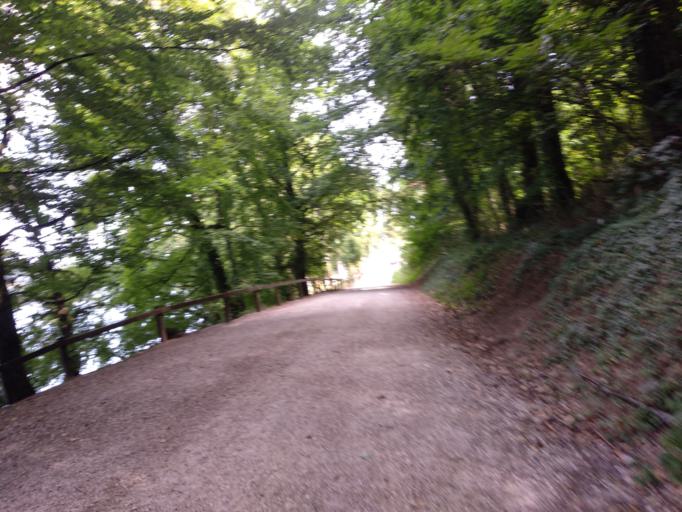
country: FR
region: Rhone-Alpes
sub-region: Departement de l'Isere
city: Charavines
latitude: 45.4408
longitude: 5.5254
